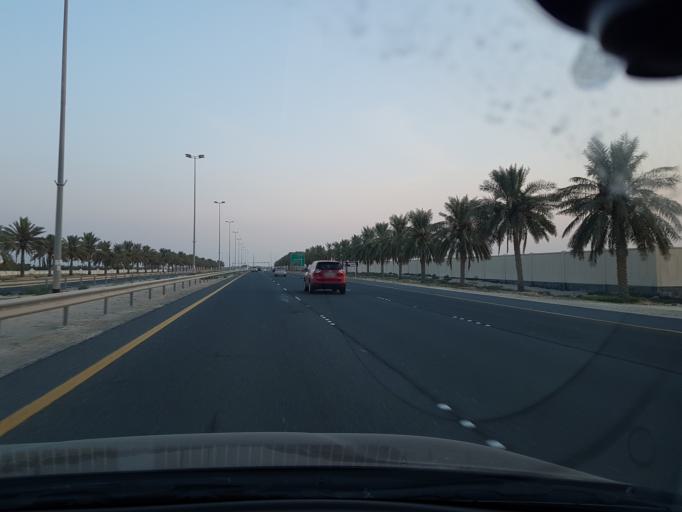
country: BH
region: Central Governorate
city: Dar Kulayb
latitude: 26.0433
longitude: 50.4998
